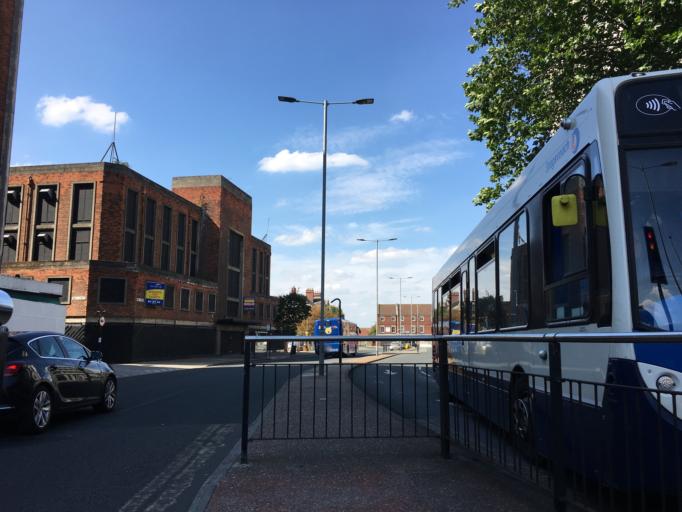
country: GB
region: England
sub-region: City of Kingston upon Hull
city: Hull
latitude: 53.7455
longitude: -0.3393
